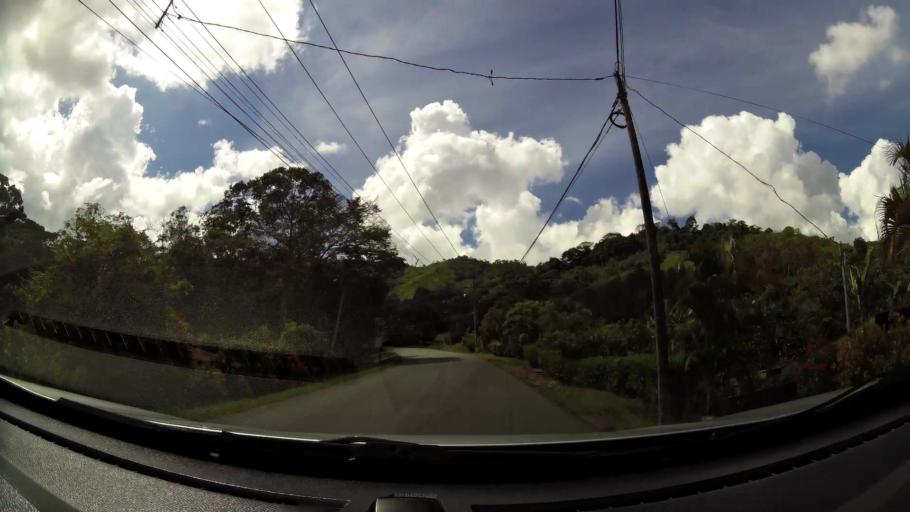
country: CR
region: San Jose
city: San Isidro
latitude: 9.3493
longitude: -83.7348
